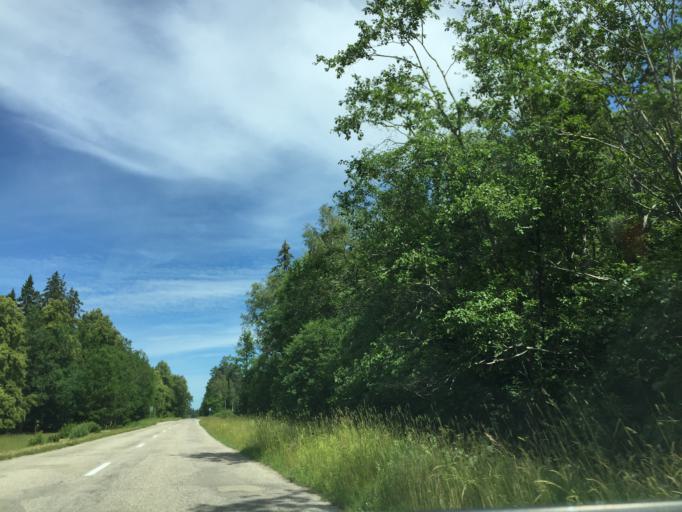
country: LV
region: Dundaga
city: Dundaga
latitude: 57.5702
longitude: 22.3067
